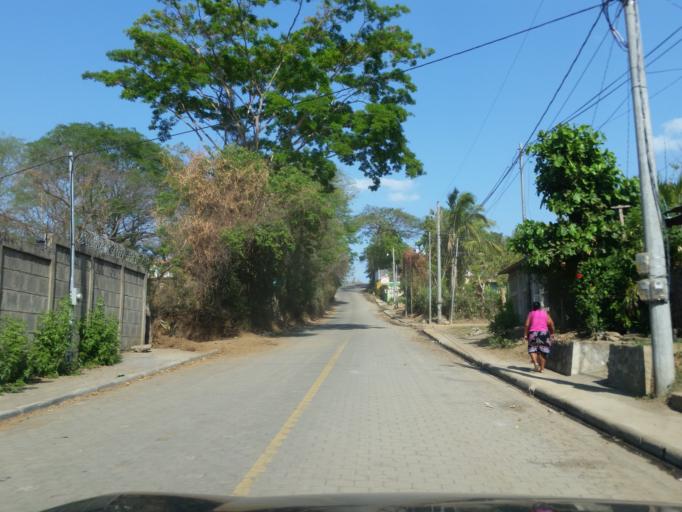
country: NI
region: Managua
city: Managua
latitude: 12.1020
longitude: -86.2933
